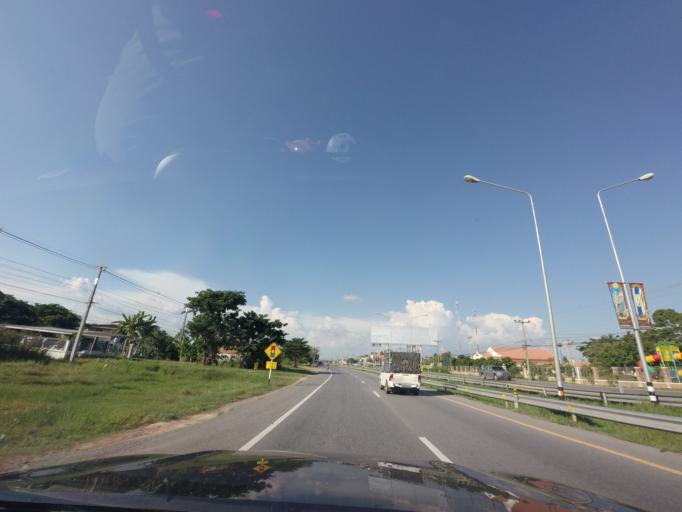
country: TH
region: Khon Kaen
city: Non Sila
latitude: 15.9613
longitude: 102.6897
